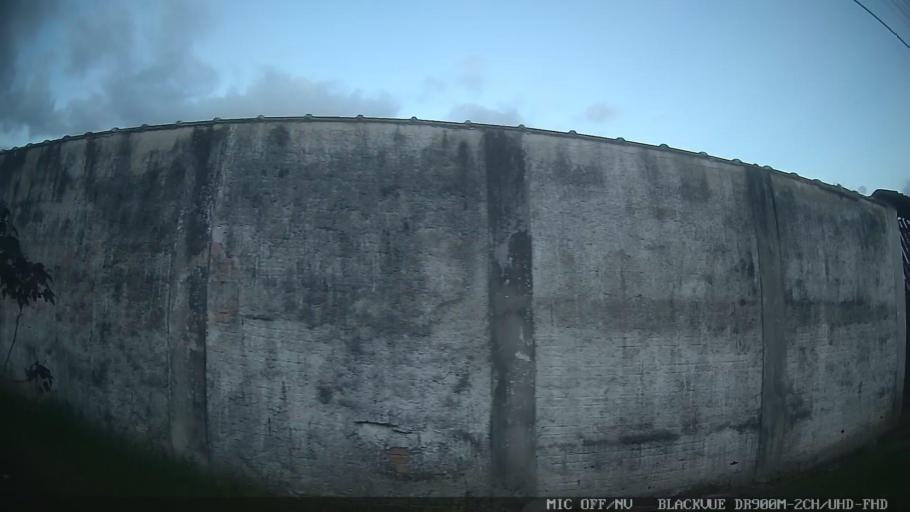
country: BR
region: Sao Paulo
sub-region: Sao Sebastiao
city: Sao Sebastiao
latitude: -23.6957
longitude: -45.4305
